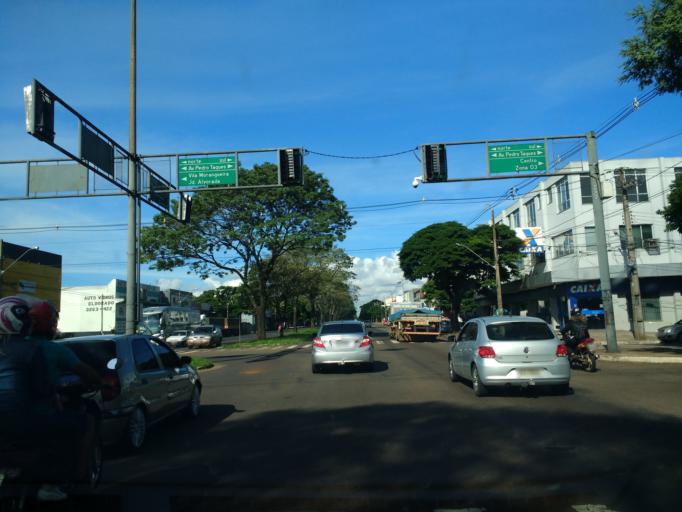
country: BR
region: Parana
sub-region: Maringa
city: Maringa
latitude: -23.4148
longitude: -51.9262
